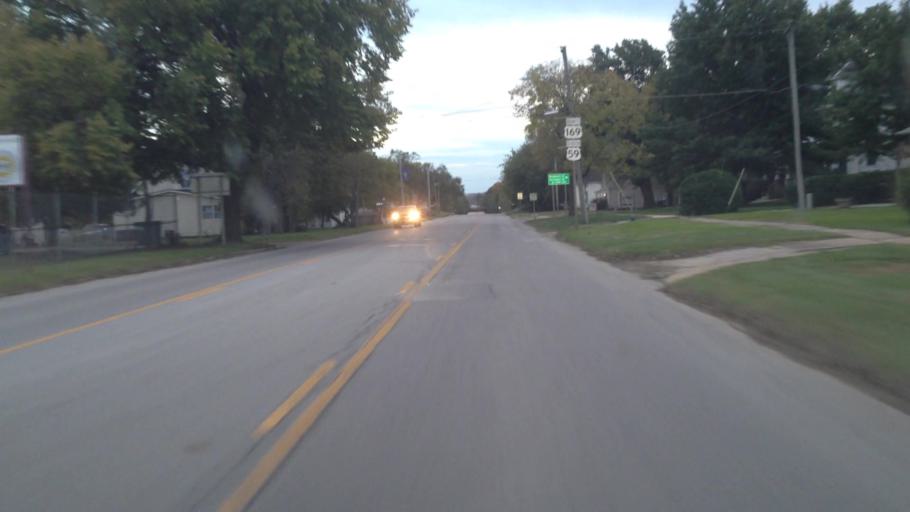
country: US
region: Kansas
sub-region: Anderson County
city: Garnett
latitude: 38.2788
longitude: -95.2493
